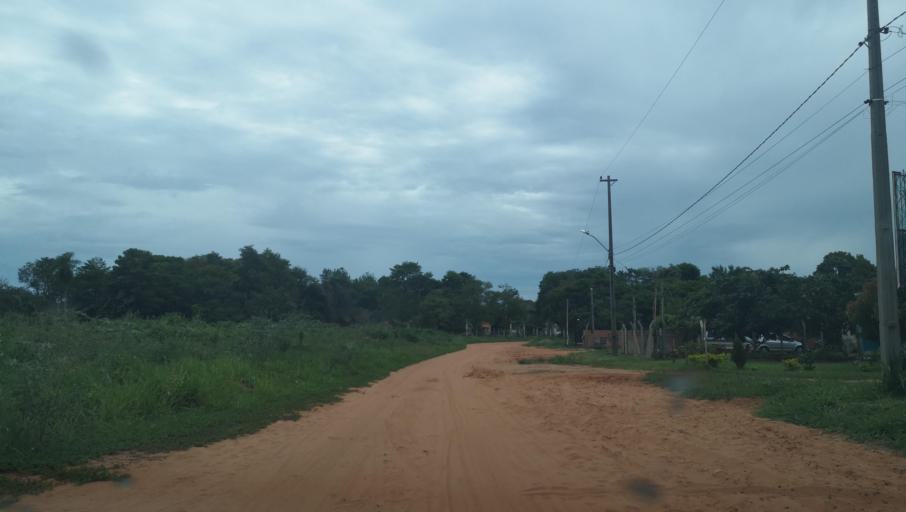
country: PY
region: San Pedro
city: Capiibary
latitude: -24.7416
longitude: -56.0209
